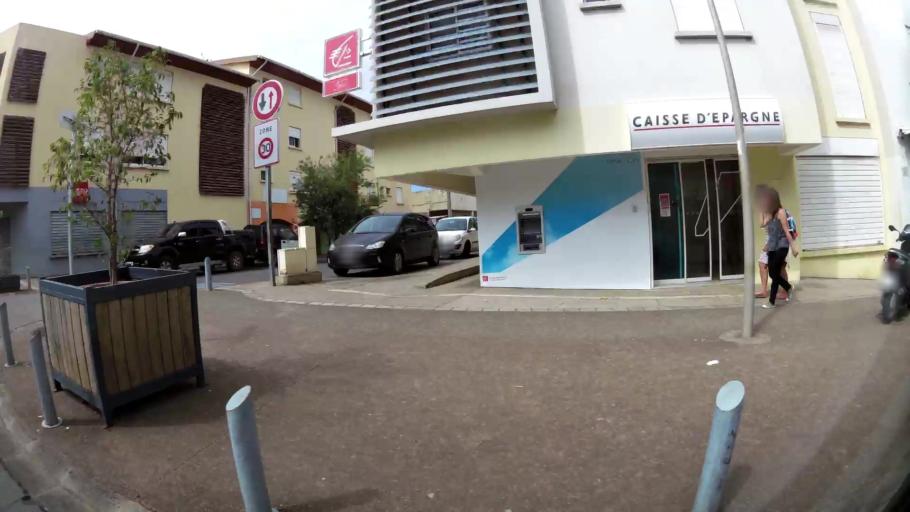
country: YT
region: Mamoudzou
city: Mamoudzou
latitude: -12.7808
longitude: 45.2327
